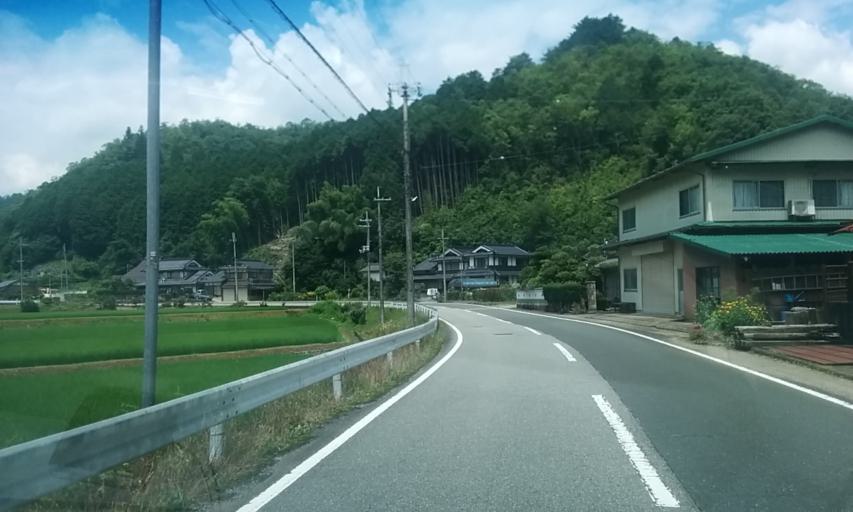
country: JP
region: Hyogo
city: Sasayama
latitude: 35.1693
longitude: 135.2570
